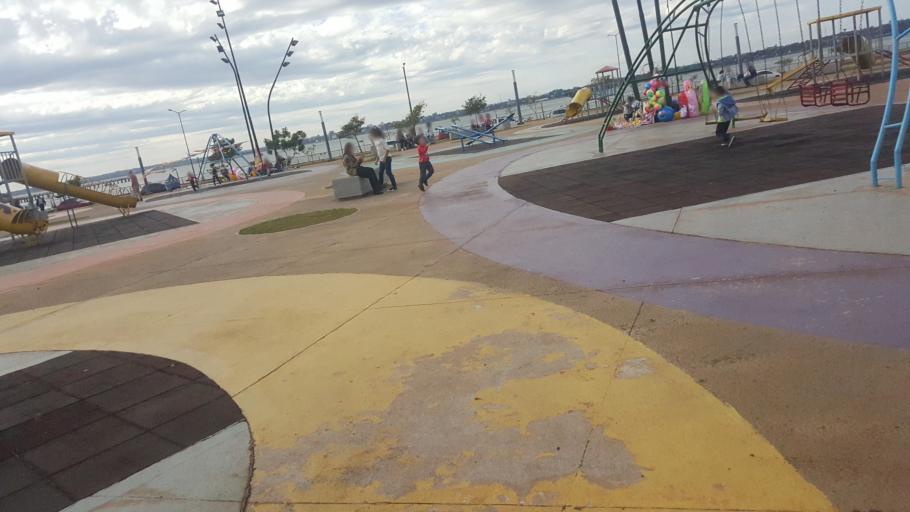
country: AR
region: Misiones
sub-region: Departamento de Capital
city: Posadas
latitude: -27.3747
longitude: -55.8837
